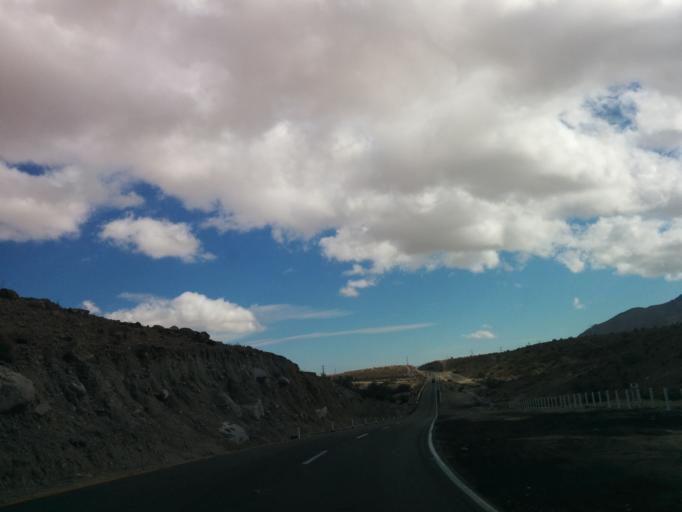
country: MX
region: Baja California
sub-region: Tecate
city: Cereso del Hongo
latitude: 32.5660
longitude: -115.9562
